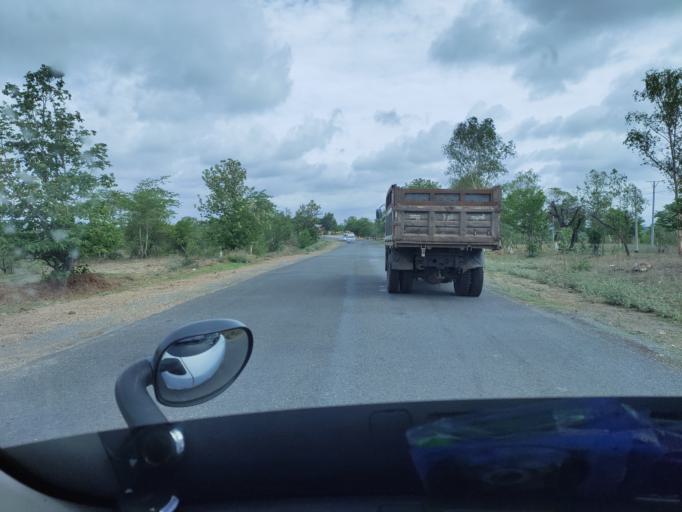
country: MM
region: Magway
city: Chauk
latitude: 20.9797
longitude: 95.0493
